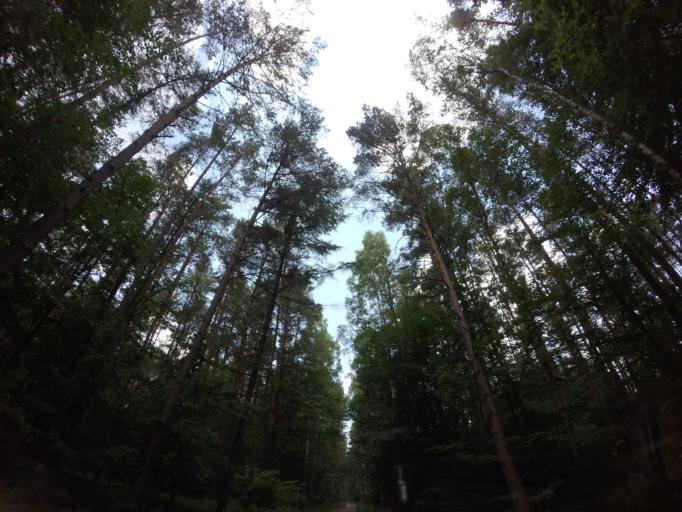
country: PL
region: West Pomeranian Voivodeship
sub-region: Powiat choszczenski
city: Bierzwnik
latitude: 53.0821
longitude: 15.6726
